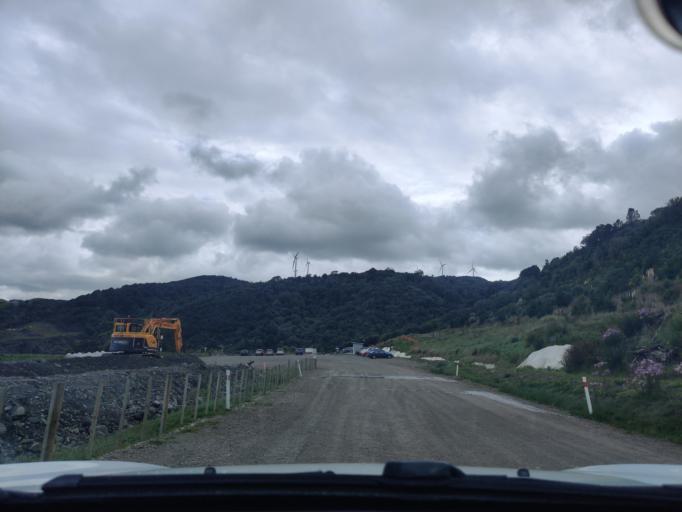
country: NZ
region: Manawatu-Wanganui
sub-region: Palmerston North City
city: Palmerston North
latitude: -40.3085
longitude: 175.7698
